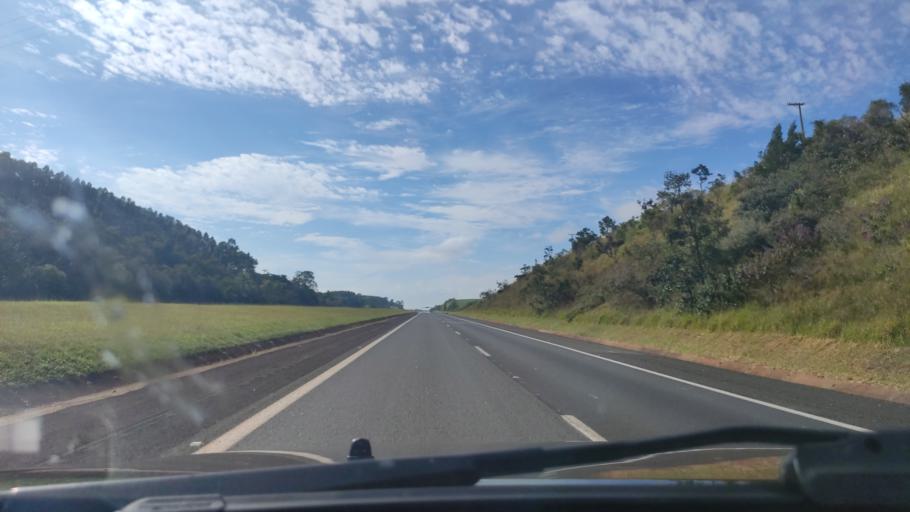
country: BR
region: Sao Paulo
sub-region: Itatinga
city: Itatinga
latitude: -23.0662
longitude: -48.5550
